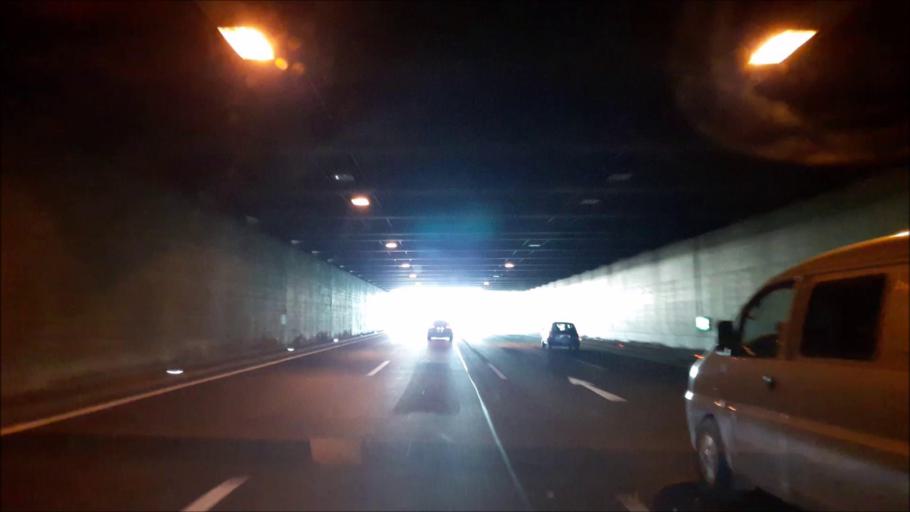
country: AT
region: Vienna
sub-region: Wien Stadt
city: Vienna
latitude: 48.2450
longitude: 16.3967
